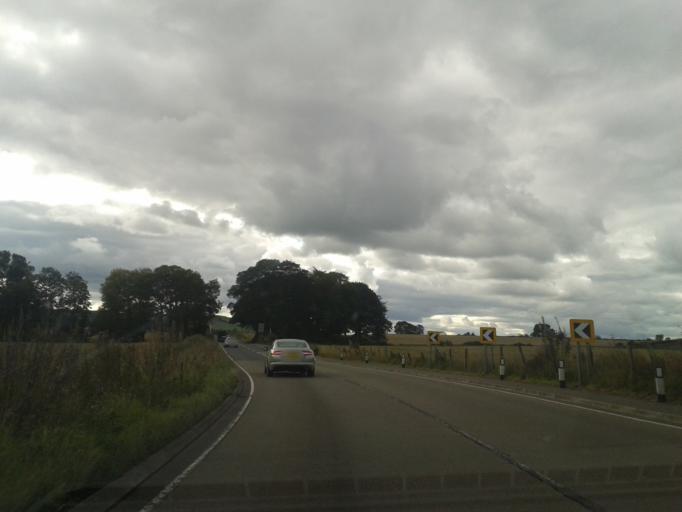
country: GB
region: Scotland
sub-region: Fife
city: Ceres
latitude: 56.3335
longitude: -2.9740
